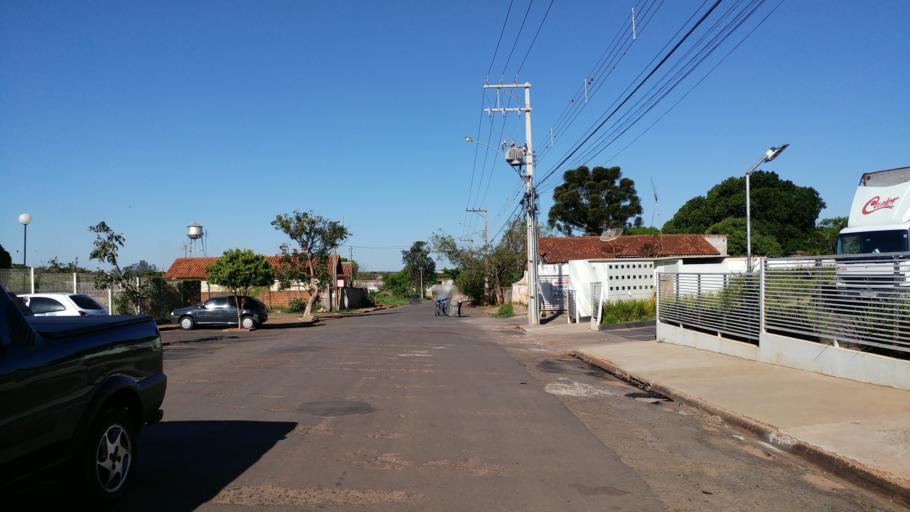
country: BR
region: Sao Paulo
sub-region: Paraguacu Paulista
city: Paraguacu Paulista
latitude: -22.4240
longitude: -50.5750
